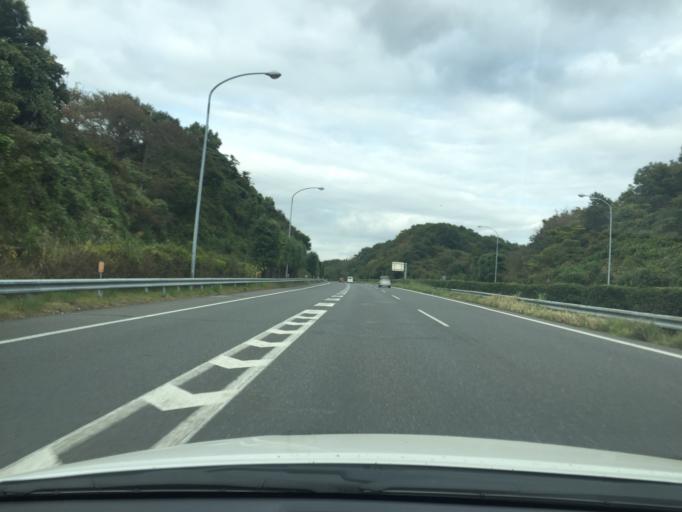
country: JP
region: Fukushima
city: Iwaki
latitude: 37.0044
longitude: 140.8109
